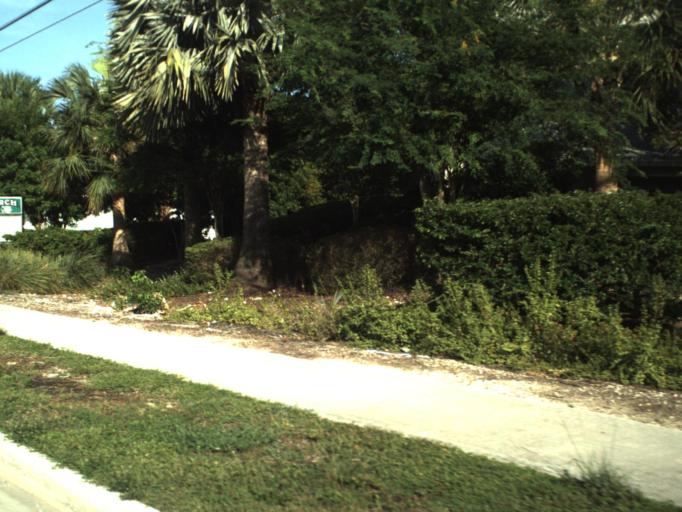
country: US
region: Florida
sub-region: Monroe County
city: Marathon
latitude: 24.7239
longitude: -81.0522
